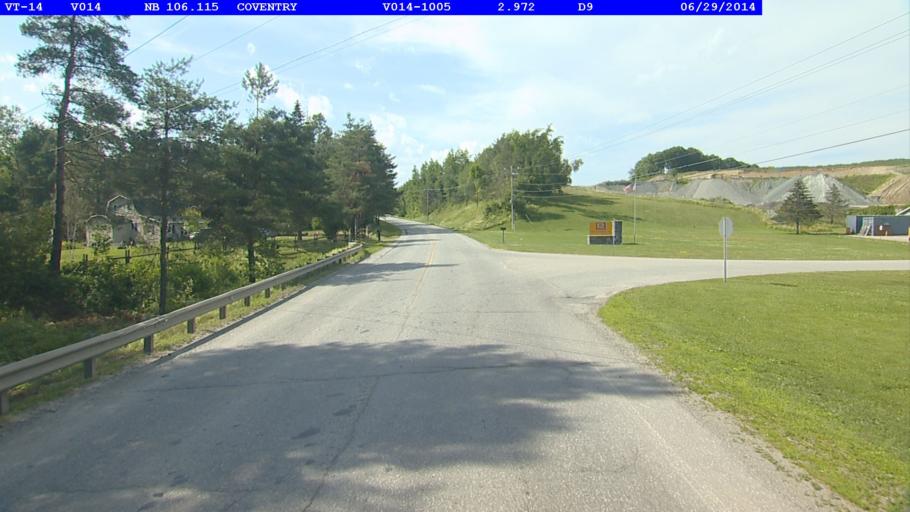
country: US
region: Vermont
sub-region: Orleans County
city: Newport
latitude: 44.9058
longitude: -72.2591
